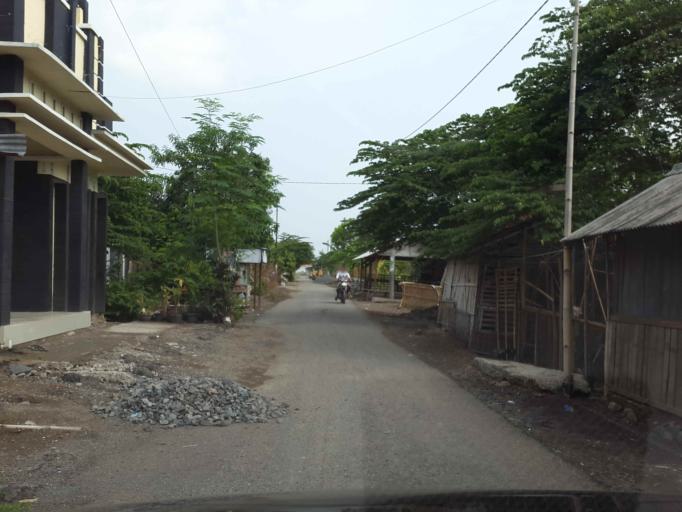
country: ID
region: Central Java
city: Ketanggungan
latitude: -6.8718
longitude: 108.8879
